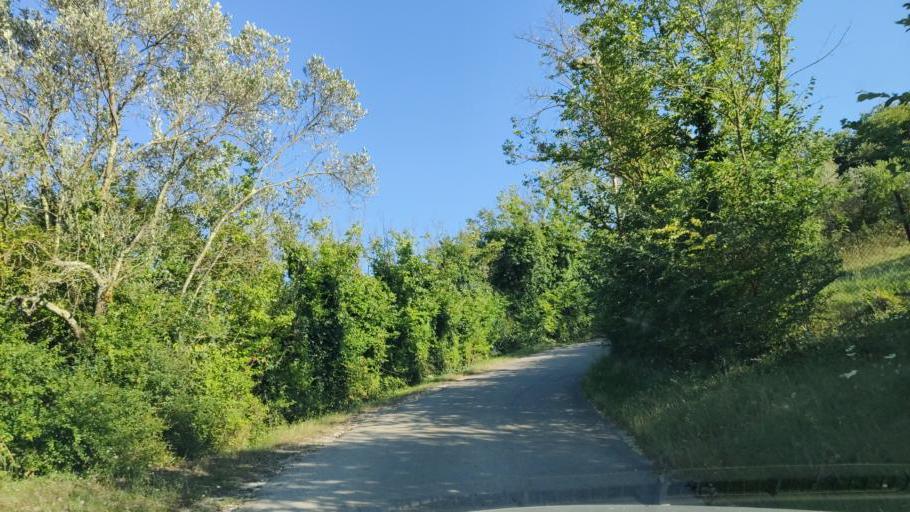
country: IT
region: Umbria
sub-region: Provincia di Terni
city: Narni
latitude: 42.5197
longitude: 12.5203
